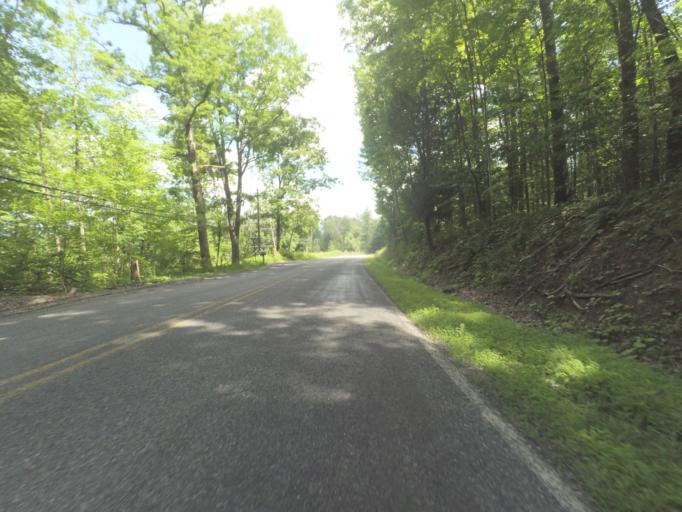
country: US
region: Pennsylvania
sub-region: Centre County
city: Stormstown
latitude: 40.7927
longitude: -78.0493
